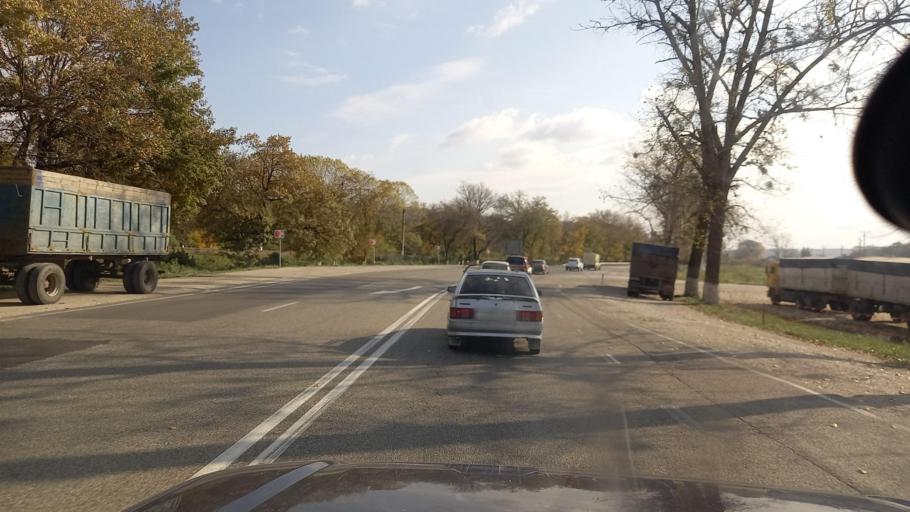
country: RU
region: Krasnodarskiy
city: Gayduk
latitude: 44.8728
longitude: 37.8288
